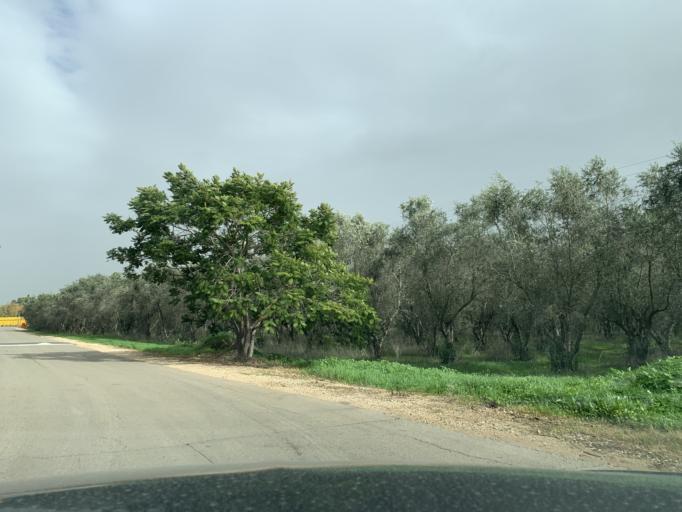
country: IL
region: Central District
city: Jaljulya
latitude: 32.1562
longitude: 34.9433
